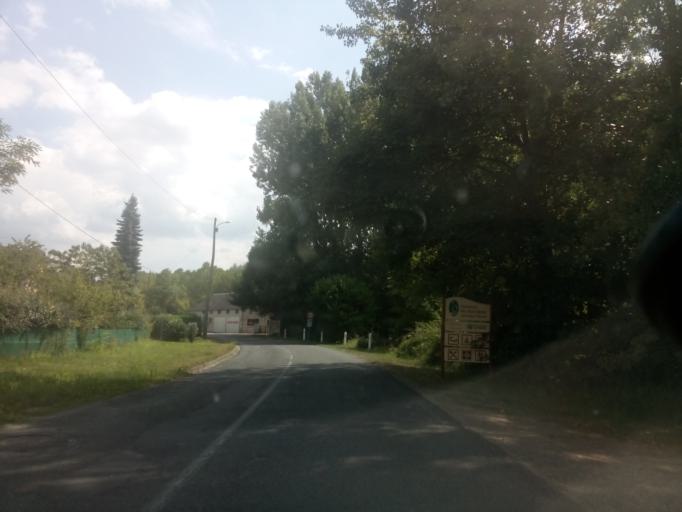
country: FR
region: Centre
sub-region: Departement d'Indre-et-Loire
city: Azay-le-Rideau
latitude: 47.2653
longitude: 0.4441
